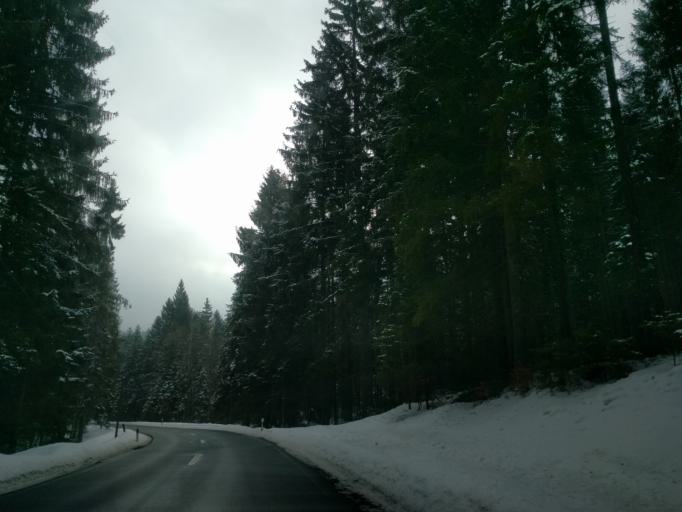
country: DE
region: Bavaria
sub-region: Lower Bavaria
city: Lindberg
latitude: 49.0484
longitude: 13.2575
